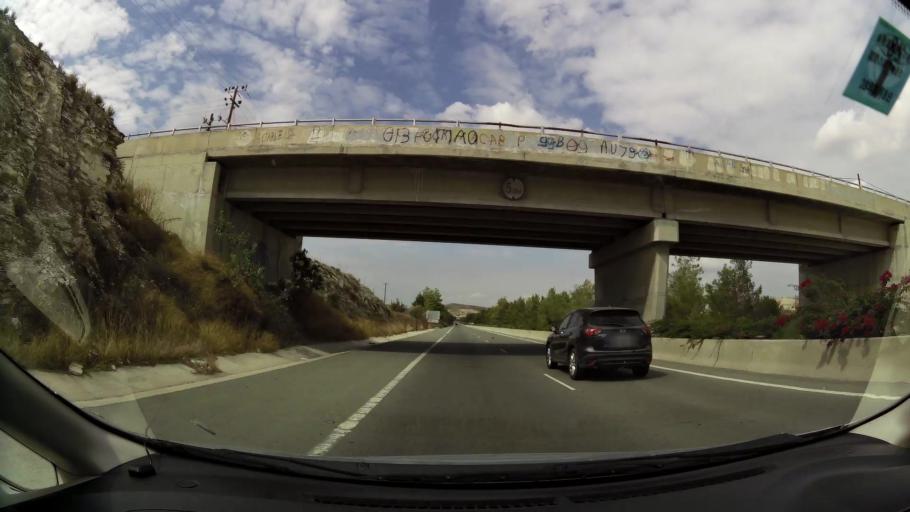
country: CY
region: Lefkosia
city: Lympia
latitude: 34.9942
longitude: 33.4471
